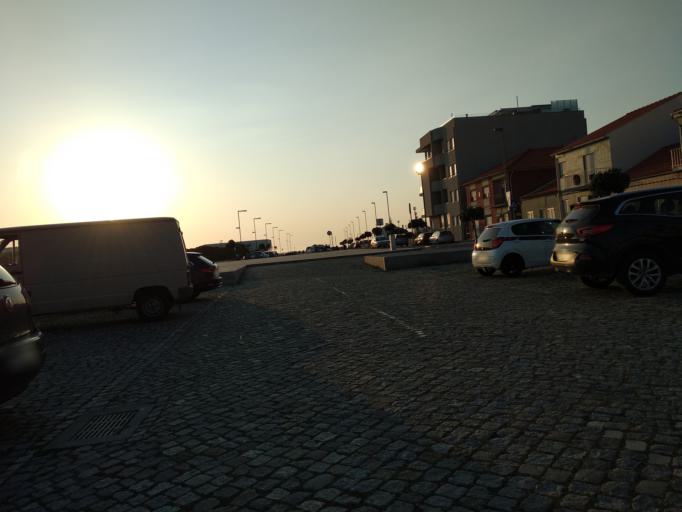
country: PT
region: Viana do Castelo
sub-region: Caminha
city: Vila Praia de Ancora
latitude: 41.8162
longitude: -8.8678
